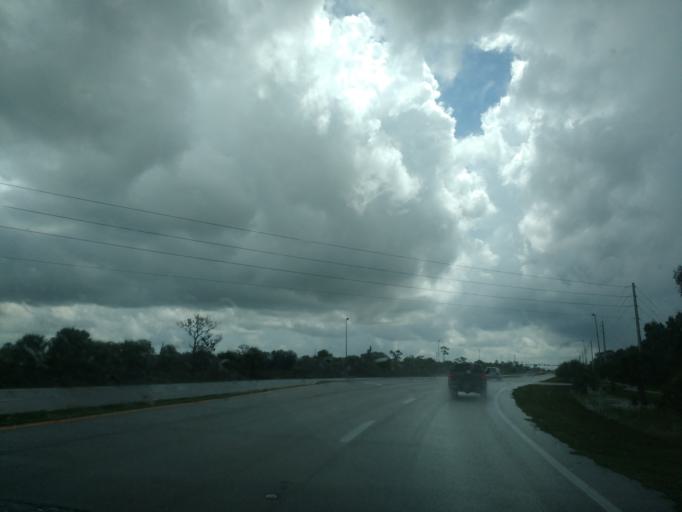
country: US
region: Florida
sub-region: Charlotte County
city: Charlotte Park
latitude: 26.8948
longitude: -82.0196
